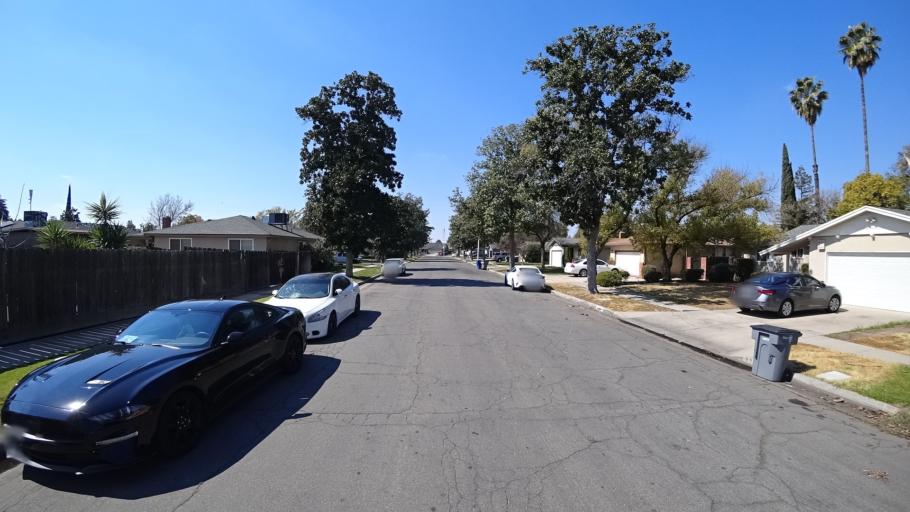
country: US
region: California
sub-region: Fresno County
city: Tarpey Village
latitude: 36.8004
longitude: -119.7320
